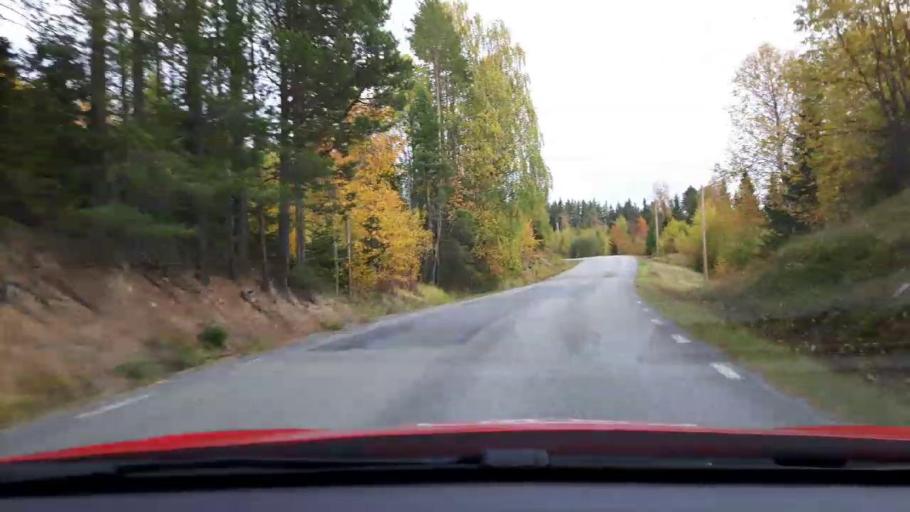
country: SE
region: Jaemtland
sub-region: Krokoms Kommun
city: Valla
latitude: 63.2614
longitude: 14.0029
